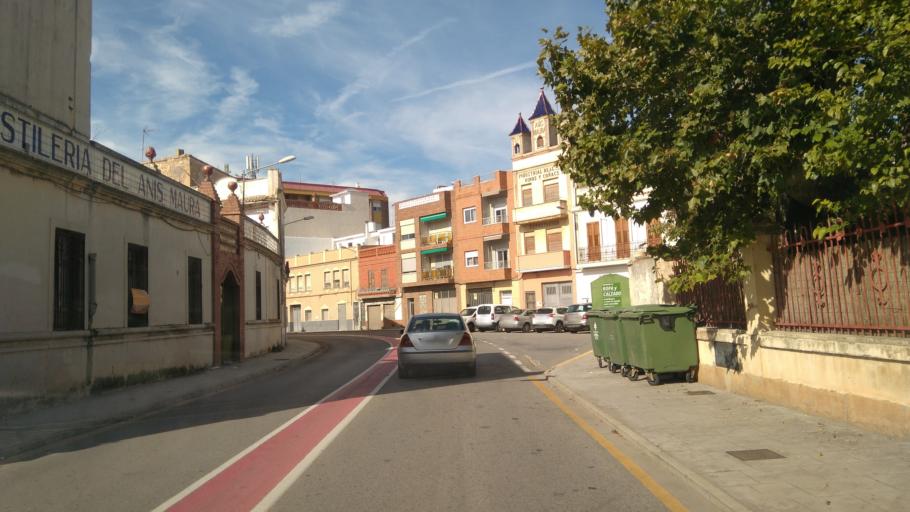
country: ES
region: Valencia
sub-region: Provincia de Valencia
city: Real de Montroi
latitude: 39.3360
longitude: -0.6083
